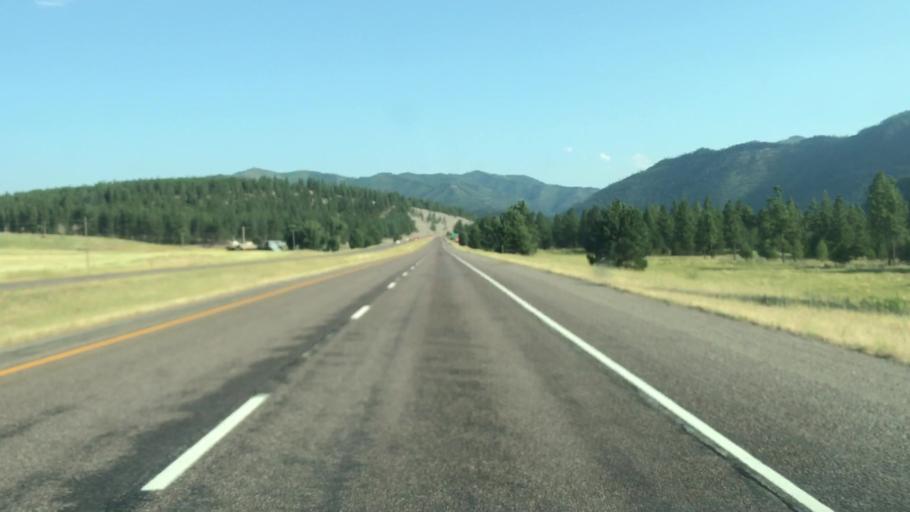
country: US
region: Montana
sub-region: Mineral County
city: Superior
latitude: 47.0329
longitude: -114.7441
